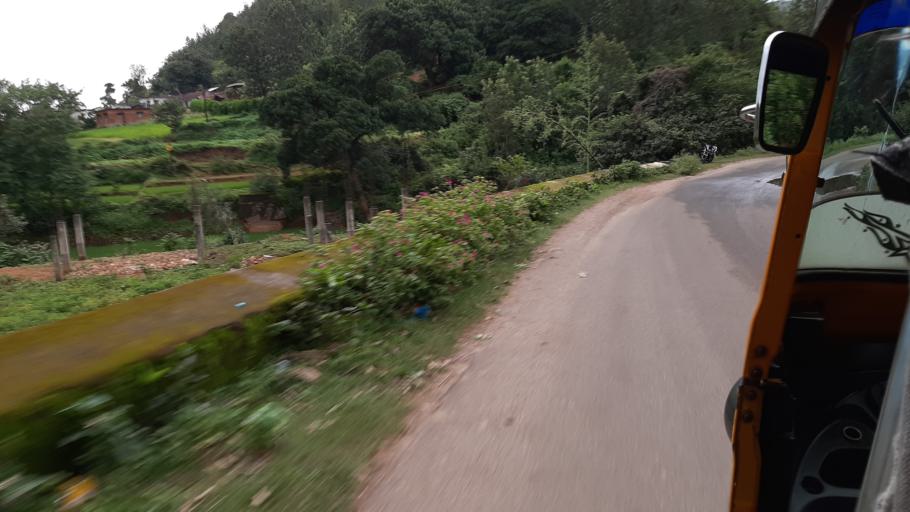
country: IN
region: Andhra Pradesh
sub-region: Vizianagaram District
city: Salur
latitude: 18.2358
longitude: 83.0041
